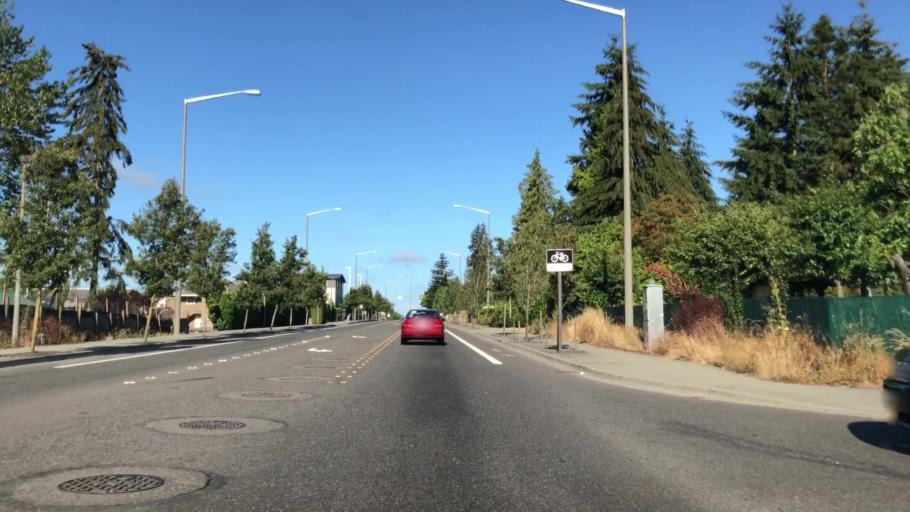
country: US
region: Washington
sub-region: King County
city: SeaTac
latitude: 47.4651
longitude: -122.2938
